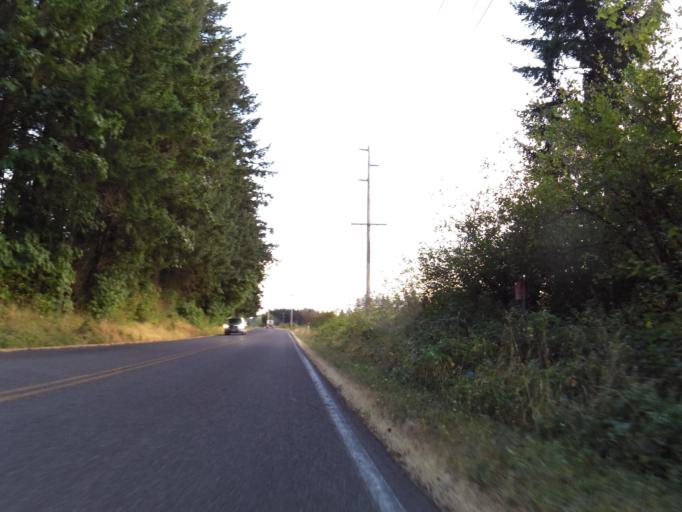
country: US
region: Washington
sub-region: Thurston County
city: Tenino
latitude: 46.8476
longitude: -122.8601
